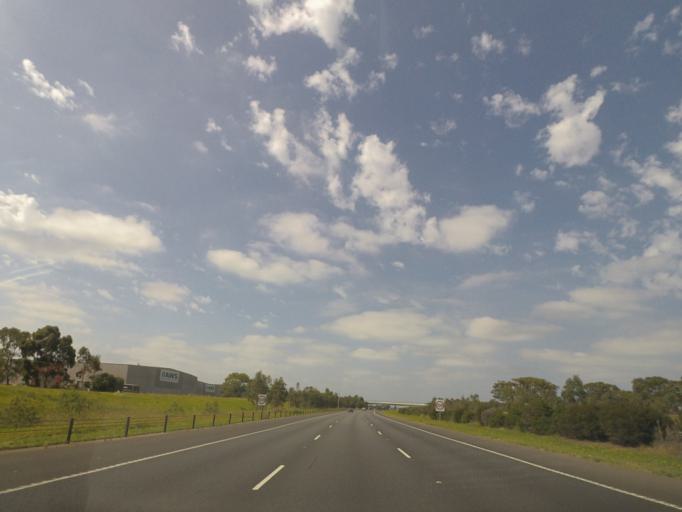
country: AU
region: Victoria
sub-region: Greater Dandenong
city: Keysborough
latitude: -38.0323
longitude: 145.1899
